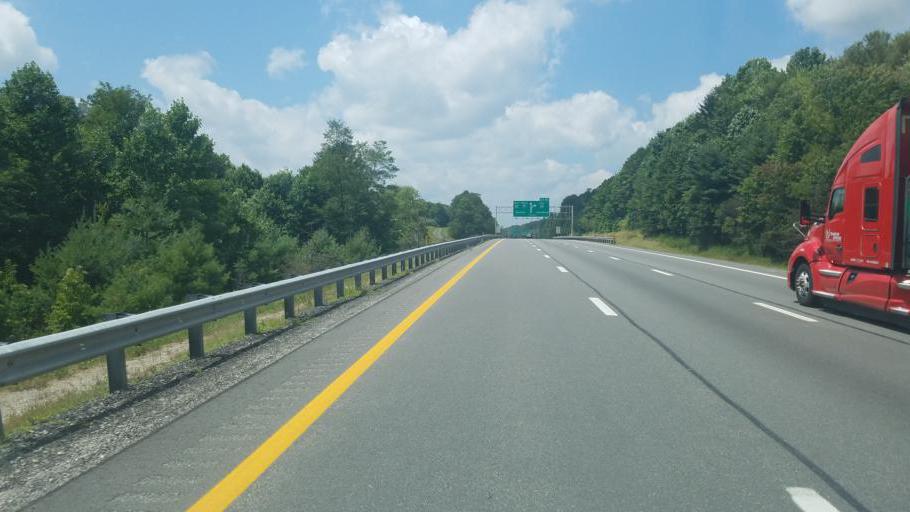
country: US
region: West Virginia
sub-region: Raleigh County
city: MacArthur
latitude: 37.7251
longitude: -81.1850
